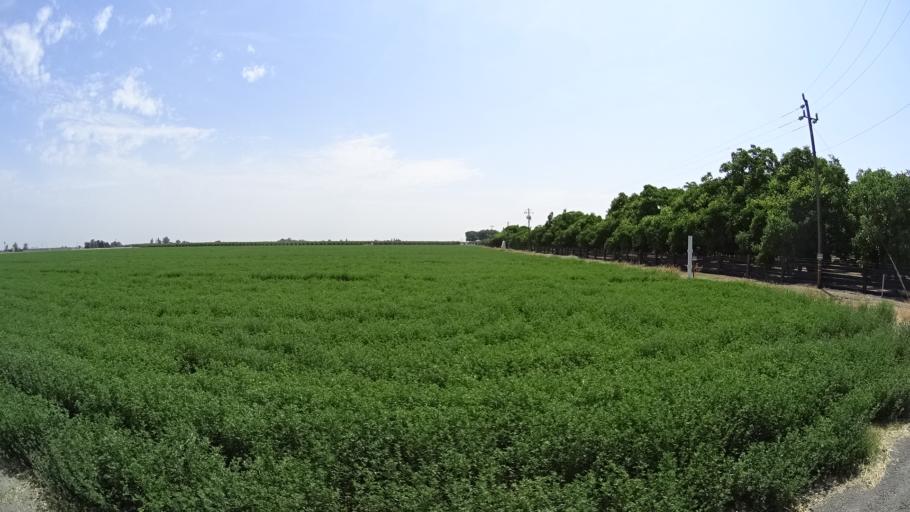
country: US
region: California
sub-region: Kings County
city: Lemoore
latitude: 36.3208
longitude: -119.7628
